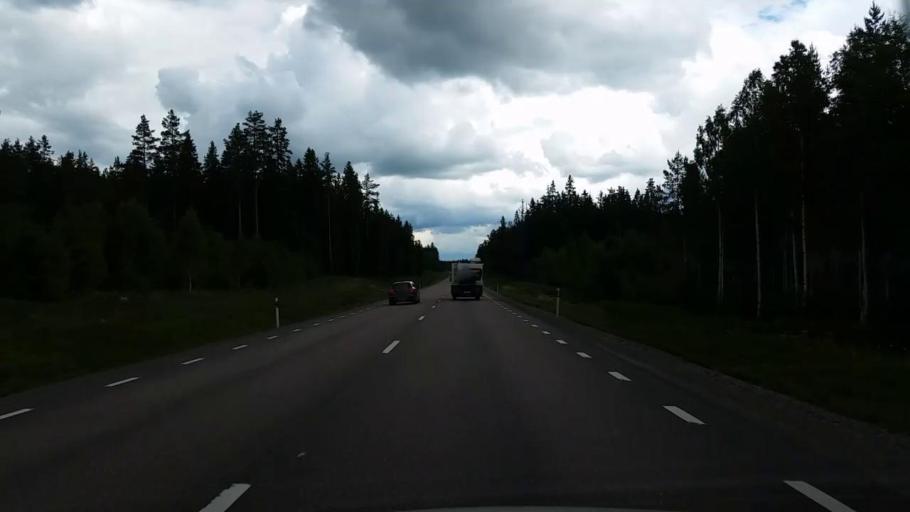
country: SE
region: Dalarna
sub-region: Avesta Kommun
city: Horndal
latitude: 60.4572
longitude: 16.4455
